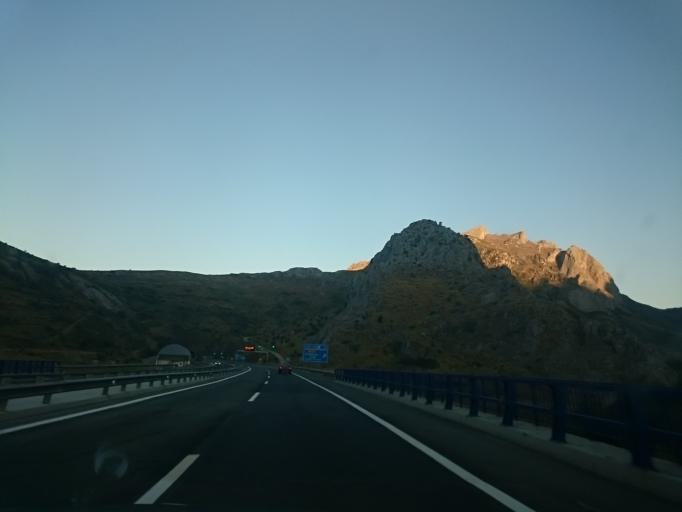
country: ES
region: Castille and Leon
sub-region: Provincia de Leon
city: Sena de Luna
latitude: 42.9204
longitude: -5.8823
